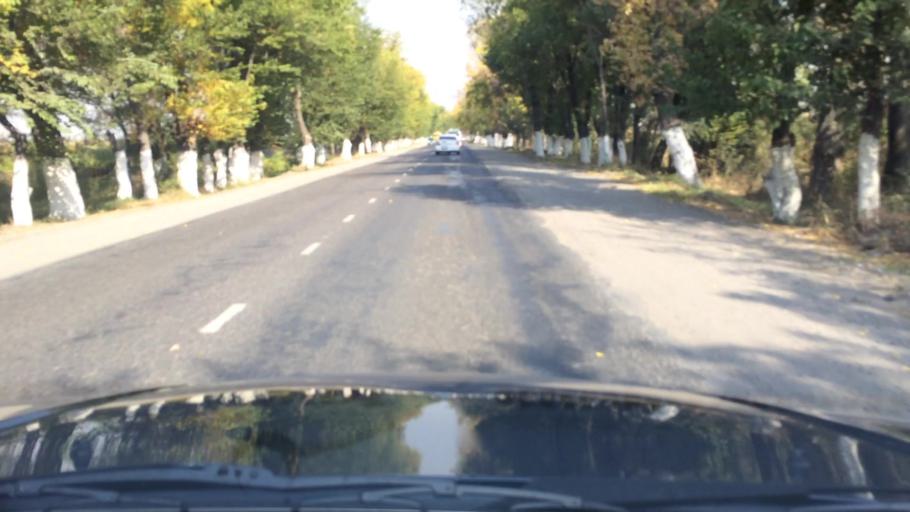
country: KG
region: Chuy
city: Lebedinovka
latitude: 42.9071
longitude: 74.6867
